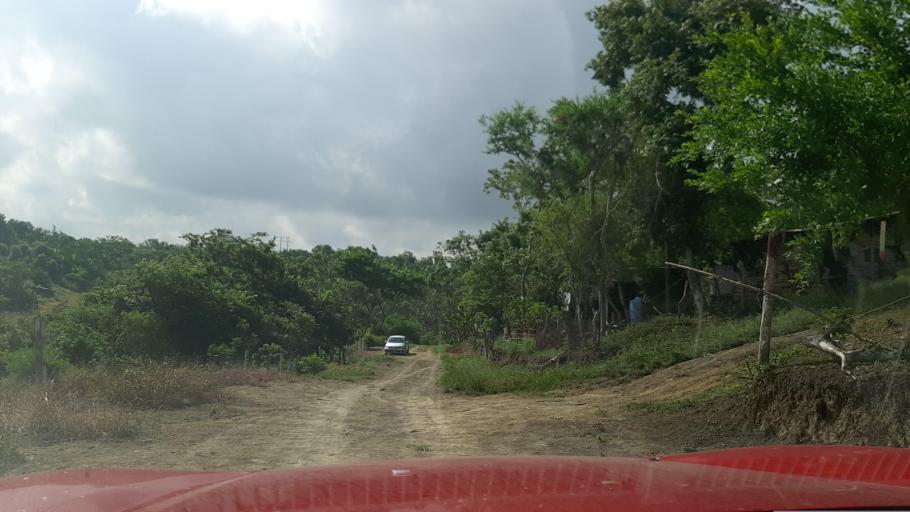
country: MX
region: Veracruz
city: Coatzintla
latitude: 20.5034
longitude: -97.4592
